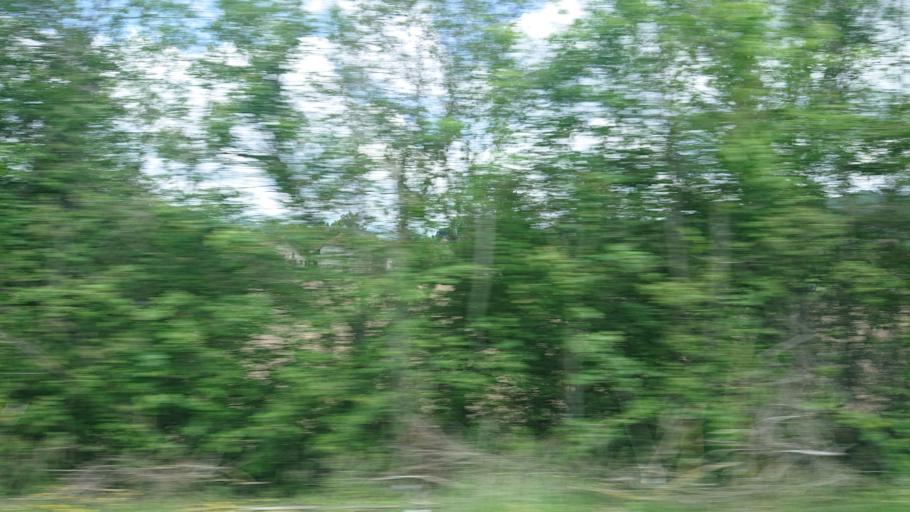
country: FR
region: Rhone-Alpes
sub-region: Departement de l'Isere
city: Chabons
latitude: 45.4266
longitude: 5.4333
